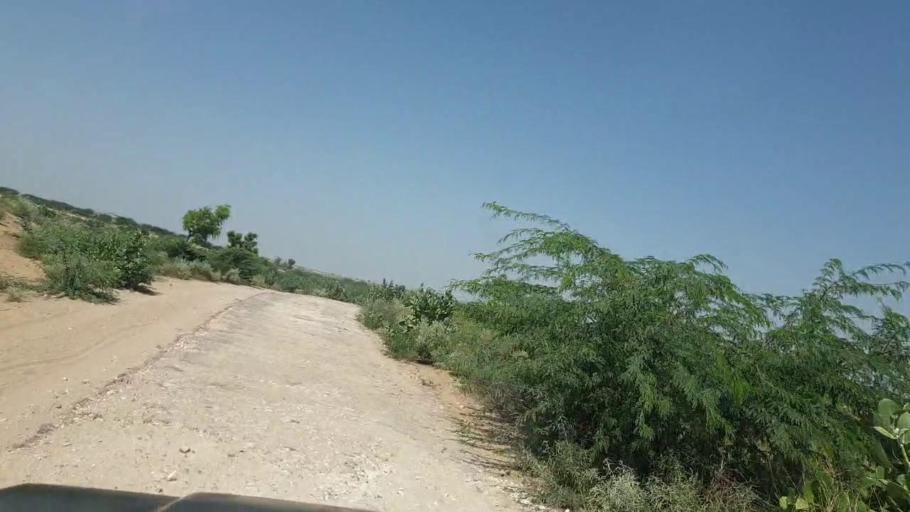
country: PK
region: Sindh
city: Chor
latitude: 25.3998
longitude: 70.3114
